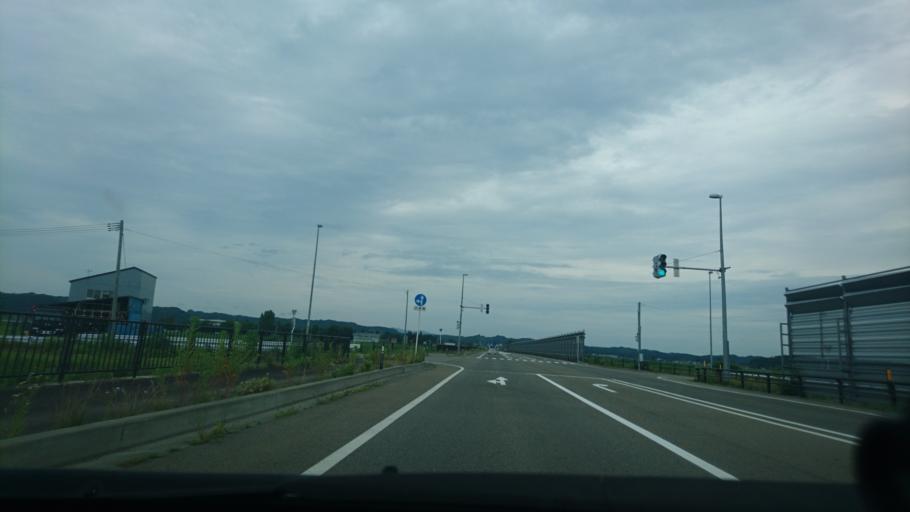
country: JP
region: Akita
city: Omagari
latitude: 39.5065
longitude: 140.3957
